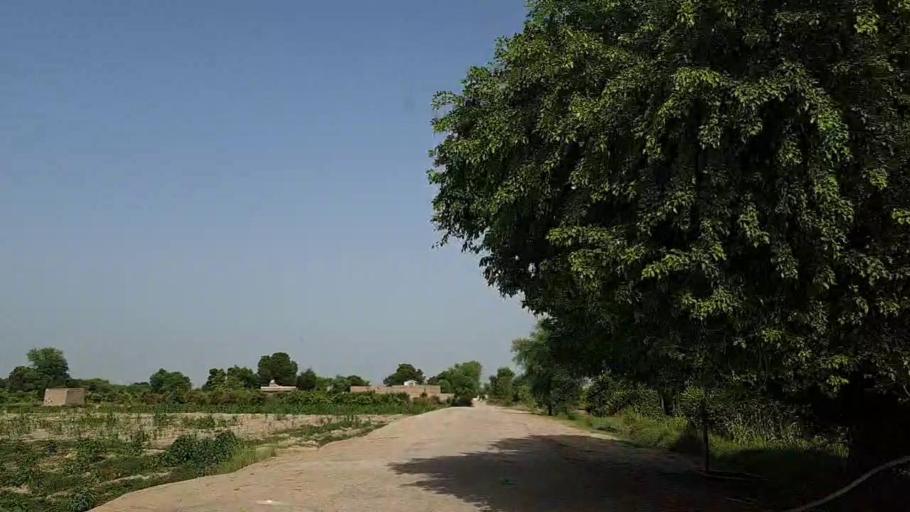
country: PK
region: Sindh
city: Kandiaro
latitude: 27.0715
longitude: 68.1561
